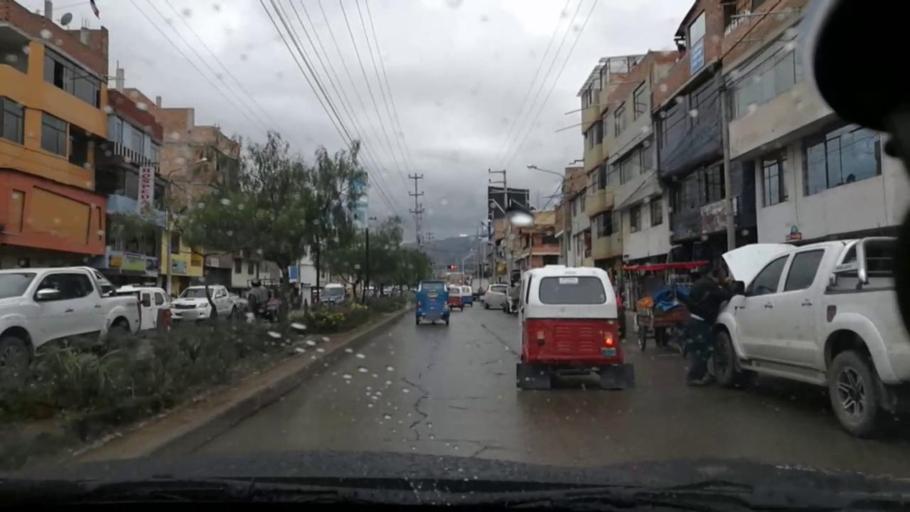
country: PE
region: Cajamarca
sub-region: Provincia de Cajamarca
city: Cajamarca
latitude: -7.1638
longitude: -78.5033
